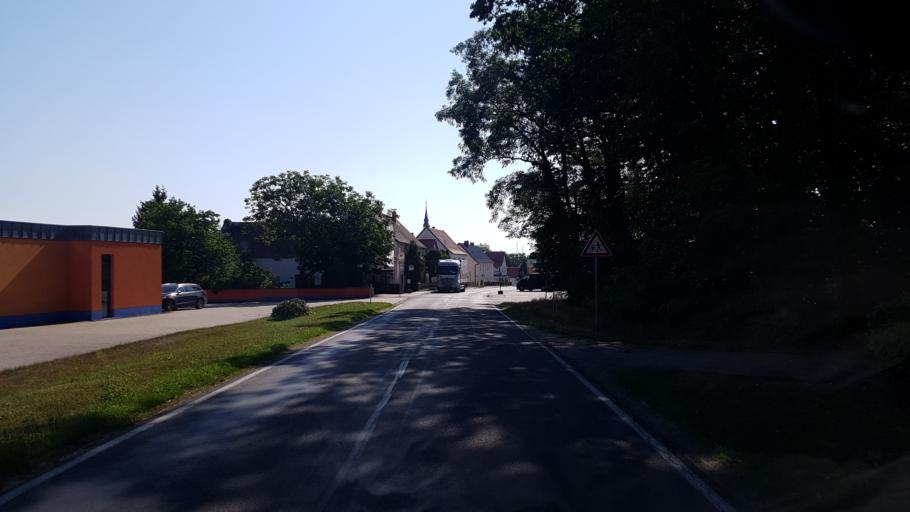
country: DE
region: Brandenburg
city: Hirschfeld
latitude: 51.3884
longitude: 13.6125
